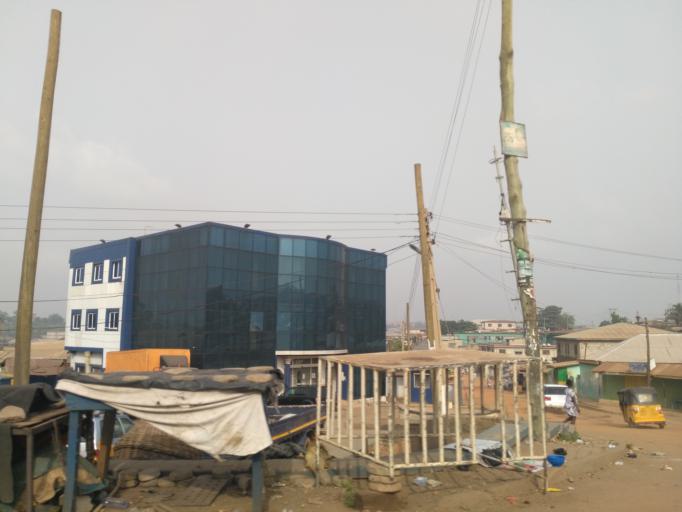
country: GH
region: Ashanti
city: Kumasi
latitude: 6.6915
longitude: -1.5956
